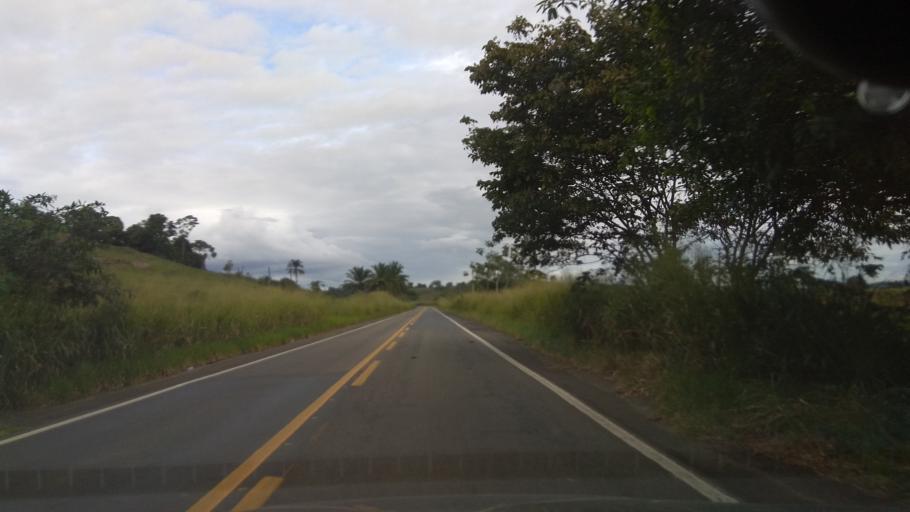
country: BR
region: Bahia
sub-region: Ipiau
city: Ipiau
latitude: -14.1843
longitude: -39.6615
